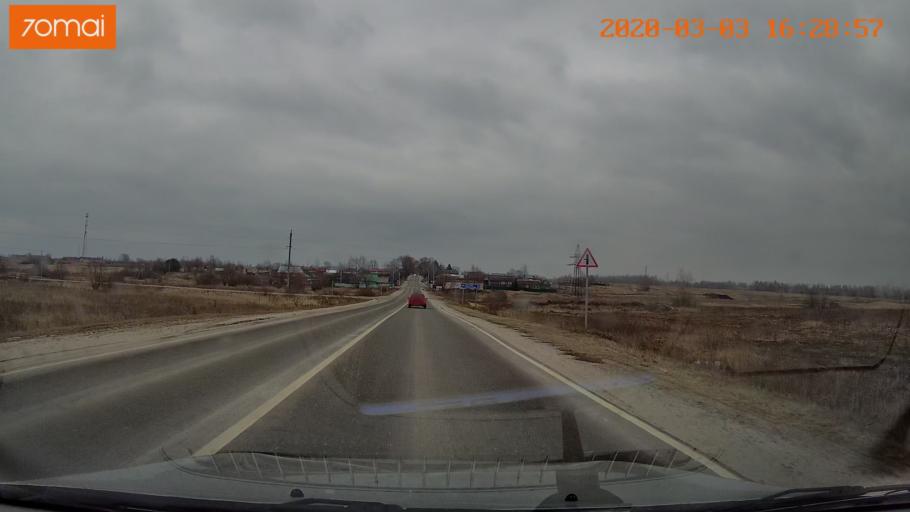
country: RU
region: Moskovskaya
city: Konobeyevo
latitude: 55.4382
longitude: 38.6953
